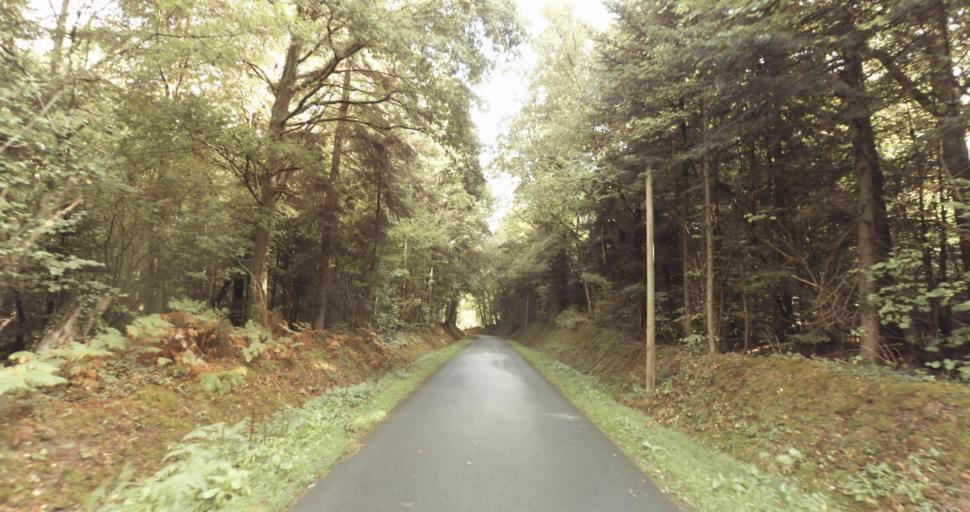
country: FR
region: Lower Normandy
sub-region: Departement de l'Orne
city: Gace
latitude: 48.8767
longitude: 0.3119
